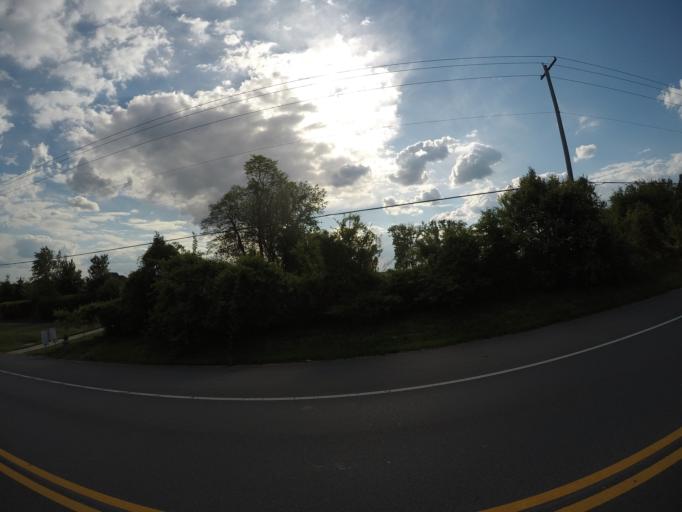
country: US
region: Maryland
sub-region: Montgomery County
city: Clarksburg
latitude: 39.2259
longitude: -77.2350
